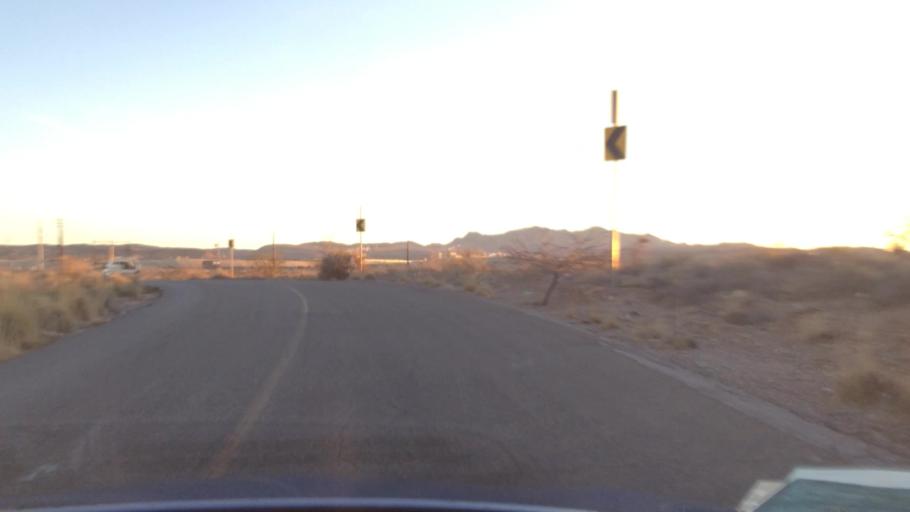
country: US
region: Nevada
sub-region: Clark County
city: Nellis Air Force Base
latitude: 36.2178
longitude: -114.8920
